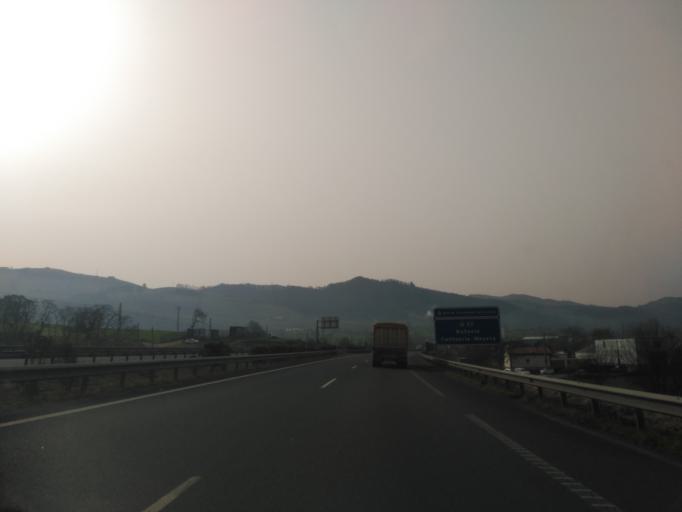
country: ES
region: Cantabria
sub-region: Provincia de Cantabria
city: Torrelavega
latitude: 43.3355
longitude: -4.0321
